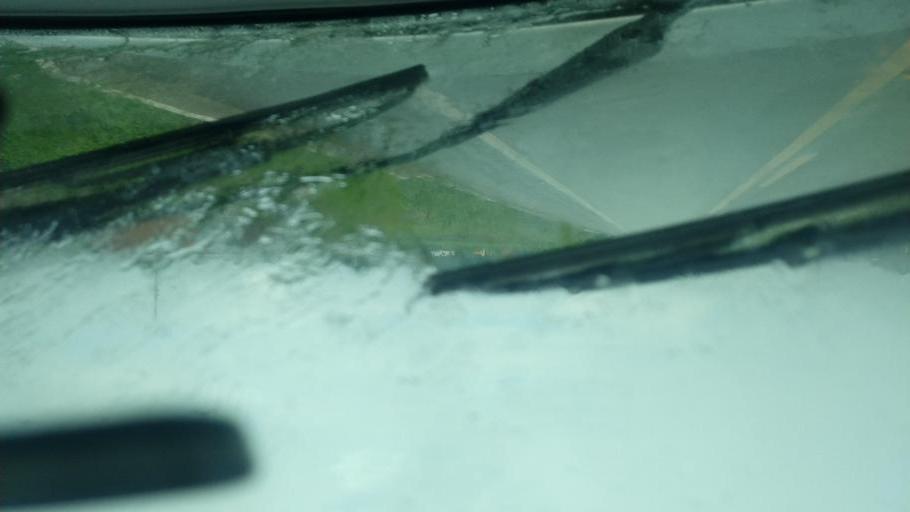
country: BR
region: Rio Grande do Norte
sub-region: Santa Cruz
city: Santa Cruz
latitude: -6.2062
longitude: -36.1892
